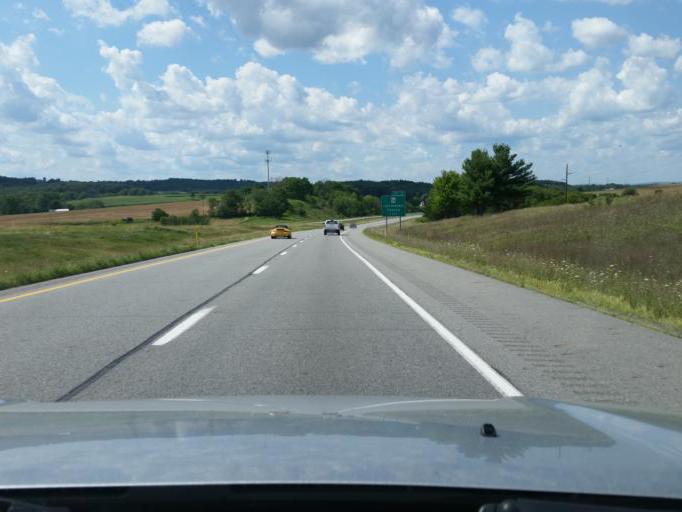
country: US
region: Pennsylvania
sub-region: Bedford County
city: Bedford
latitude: 40.0765
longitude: -78.5244
